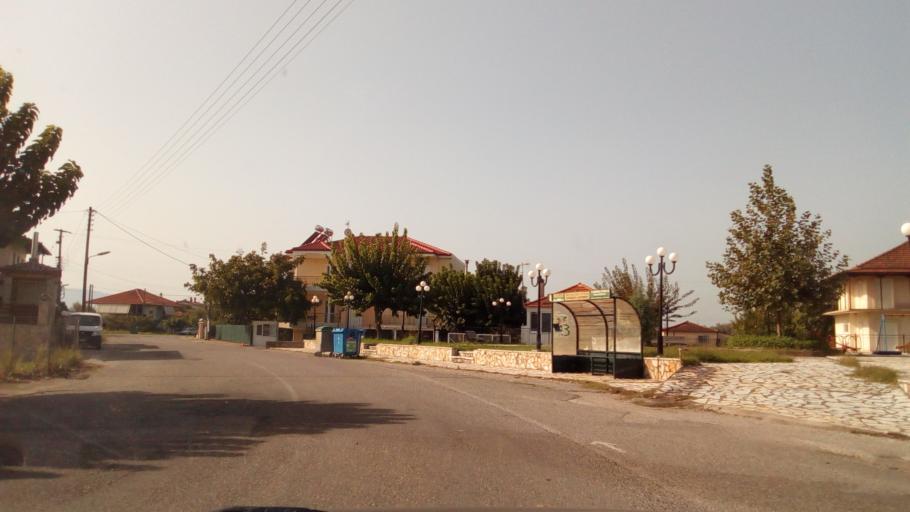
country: GR
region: West Greece
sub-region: Nomos Aitolias kai Akarnanias
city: Nafpaktos
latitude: 38.4001
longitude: 21.8988
